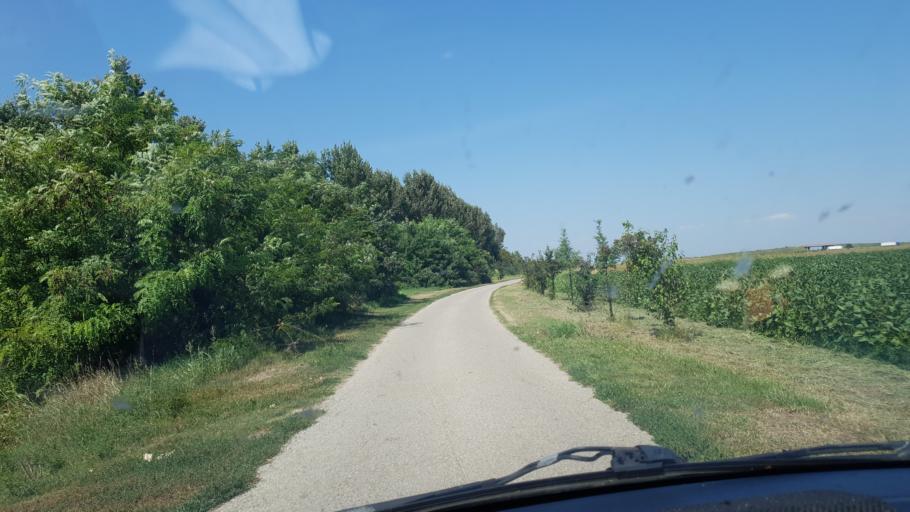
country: RS
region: Autonomna Pokrajina Vojvodina
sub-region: Juznobacki Okrug
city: Kovilj
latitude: 45.2017
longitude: 20.0630
